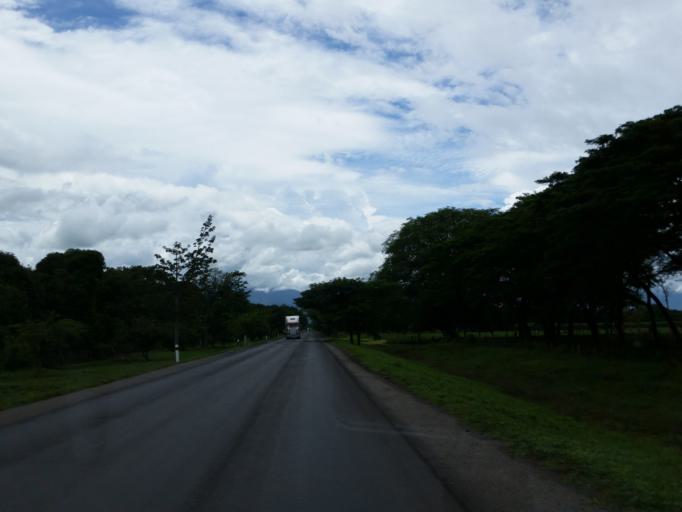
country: NI
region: Chinandega
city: Somotillo
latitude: 12.8521
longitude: -86.8738
